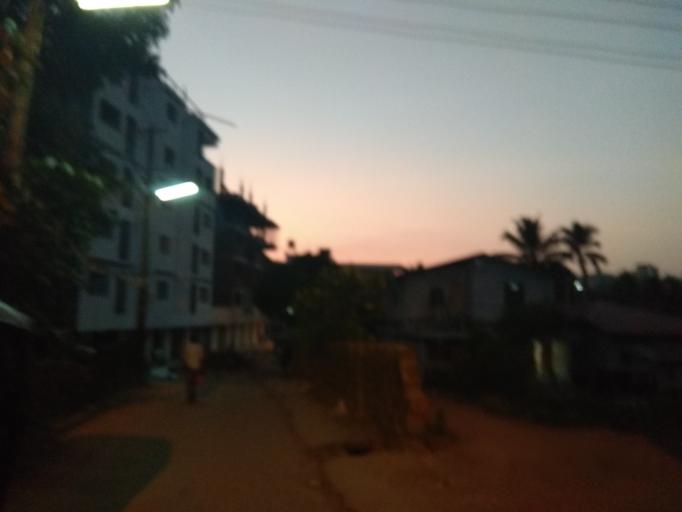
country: IN
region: Karnataka
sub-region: Dakshina Kannada
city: Mangalore
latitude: 12.8967
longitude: 74.8543
